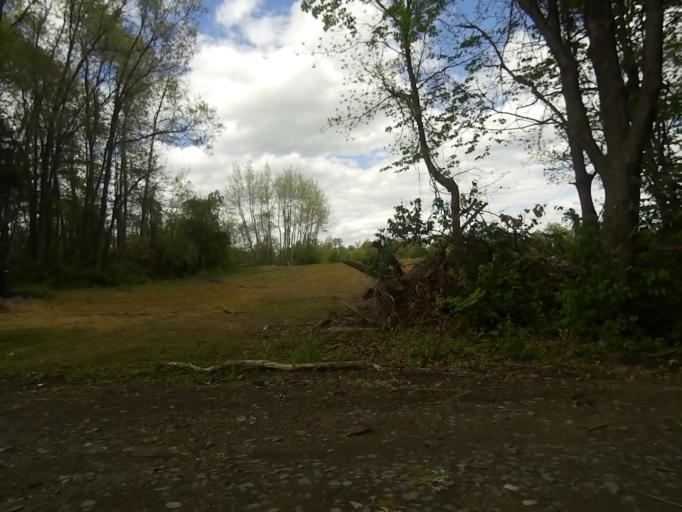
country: US
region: Pennsylvania
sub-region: Centre County
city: Park Forest Village
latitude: 40.8304
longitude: -77.9003
